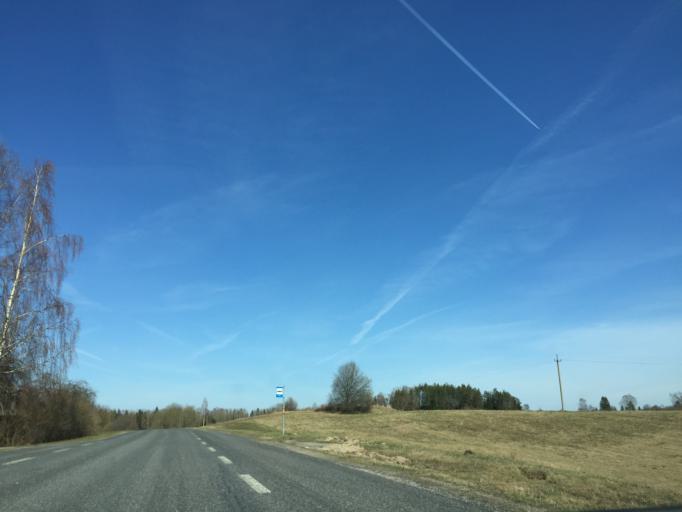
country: EE
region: Vorumaa
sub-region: Antsla vald
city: Vana-Antsla
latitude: 57.9933
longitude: 26.4166
